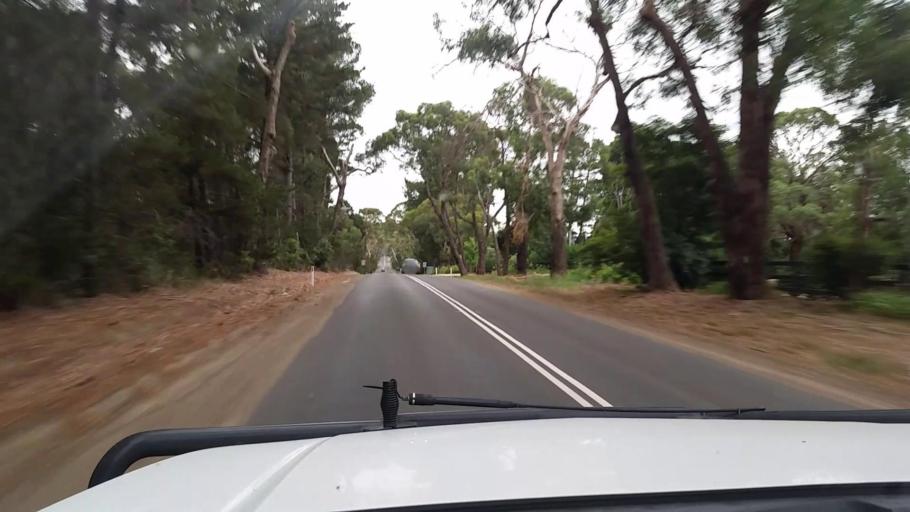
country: AU
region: Victoria
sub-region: Mornington Peninsula
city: Hastings
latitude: -38.3191
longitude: 145.1456
